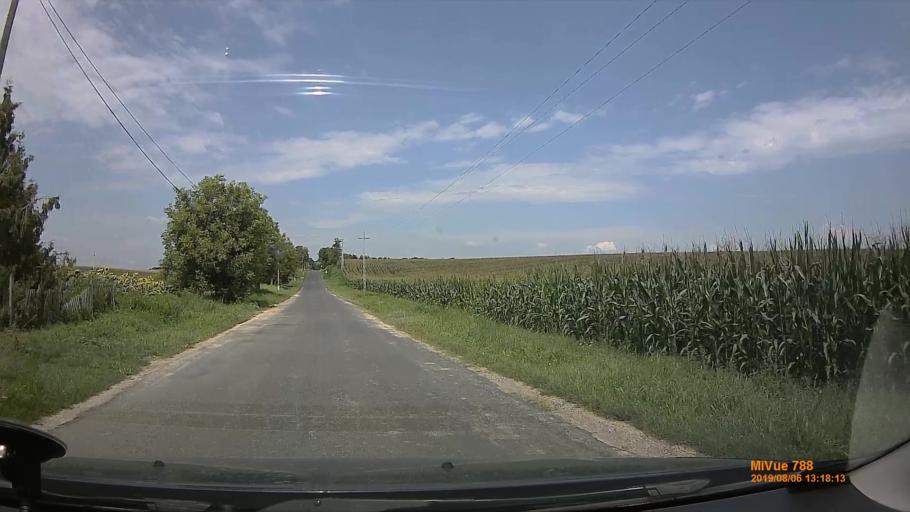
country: HU
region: Zala
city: Pacsa
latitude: 46.6314
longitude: 17.0609
